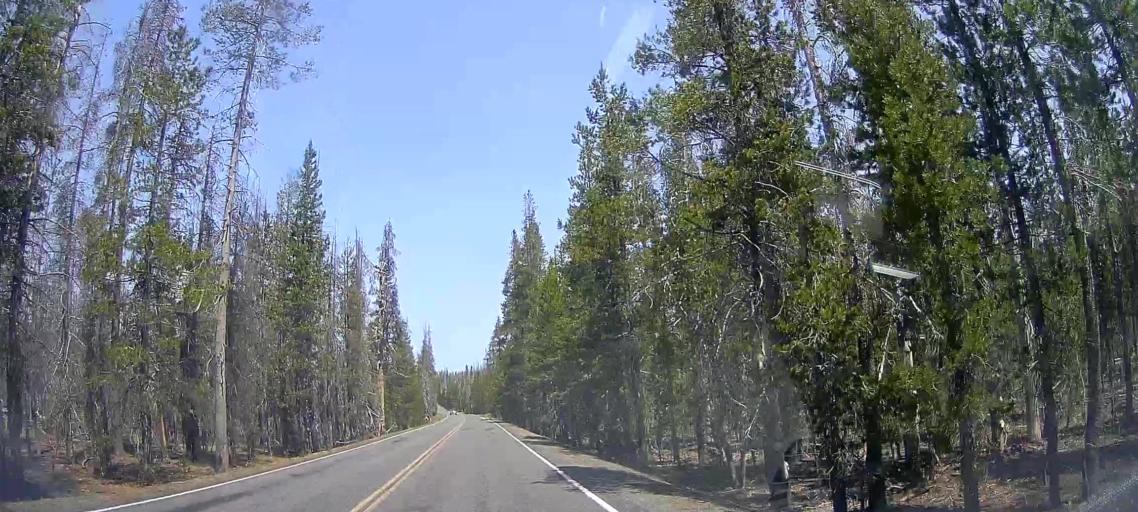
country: US
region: Oregon
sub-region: Lane County
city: Oakridge
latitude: 43.0439
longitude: -122.1182
